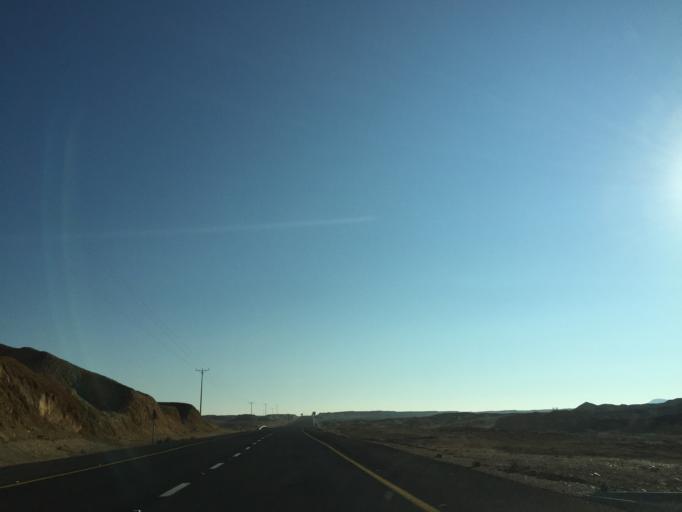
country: IL
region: Southern District
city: Mitzpe Ramon
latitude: 30.2782
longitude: 35.0078
